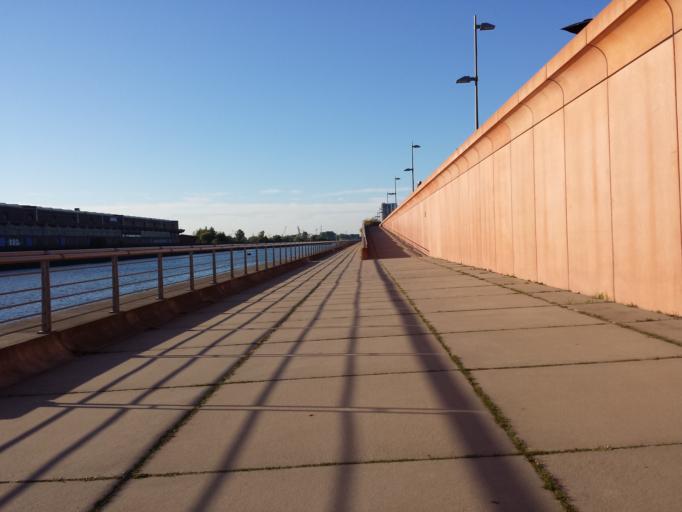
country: DE
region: Bremen
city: Bremen
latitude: 53.0903
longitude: 8.7737
